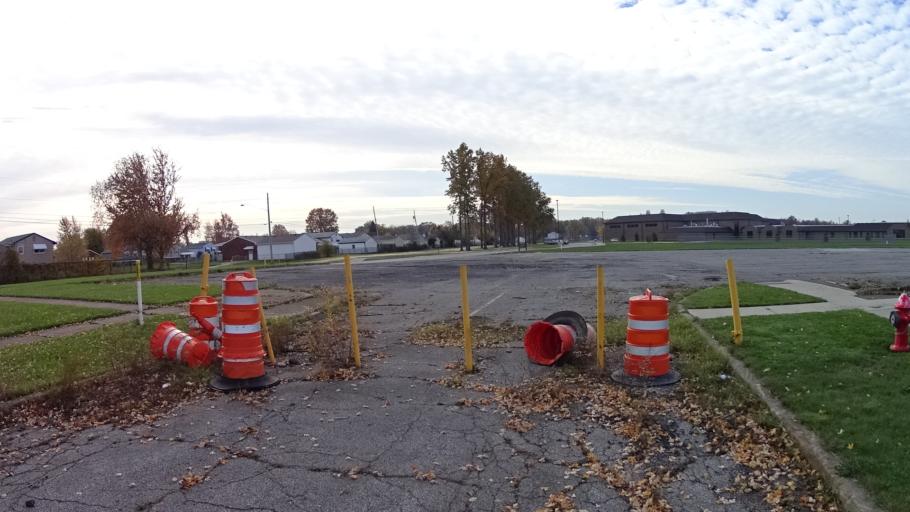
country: US
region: Ohio
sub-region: Lorain County
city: Sheffield
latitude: 41.4304
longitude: -82.1153
